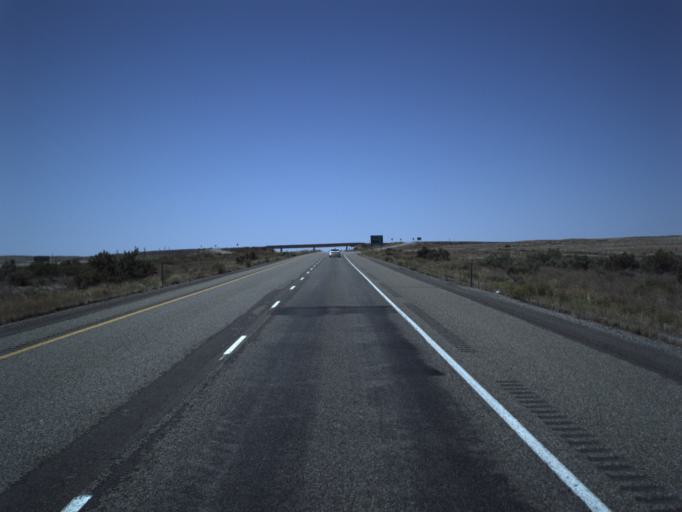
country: US
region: Colorado
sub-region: Mesa County
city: Loma
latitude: 39.1187
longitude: -109.1768
